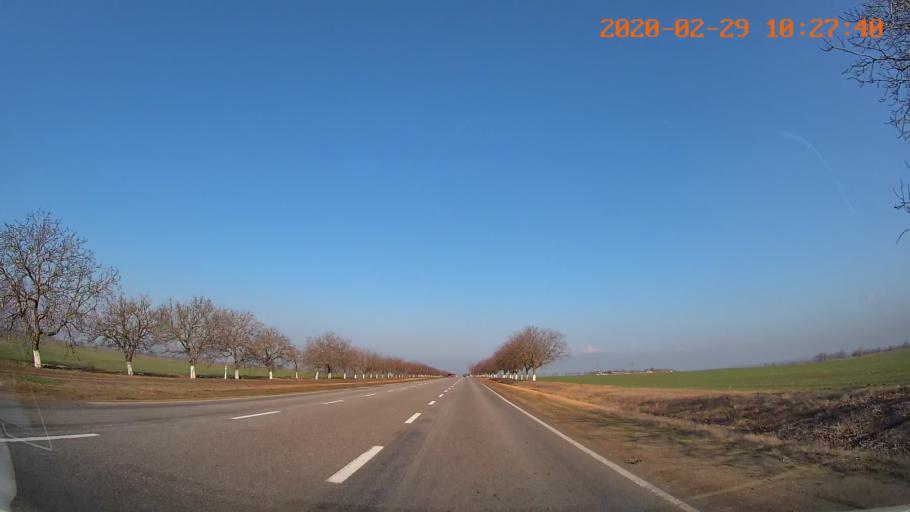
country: MD
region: Telenesti
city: Tiraspolul Nou
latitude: 46.8994
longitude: 29.5963
